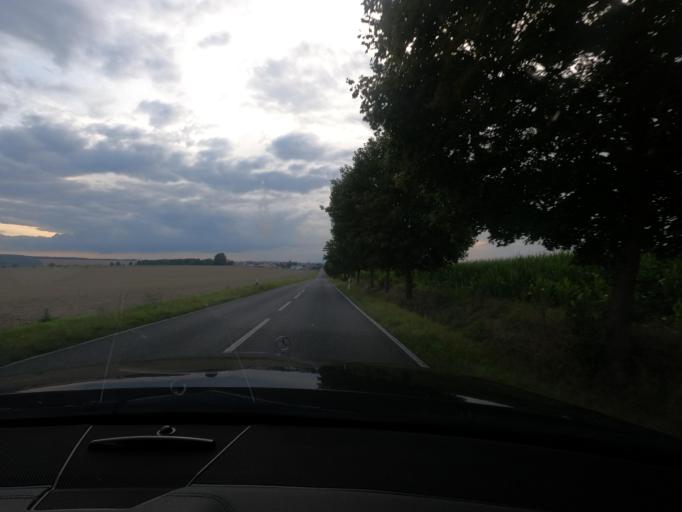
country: DE
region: Thuringia
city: Breitenworbis
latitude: 51.3990
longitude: 10.4205
